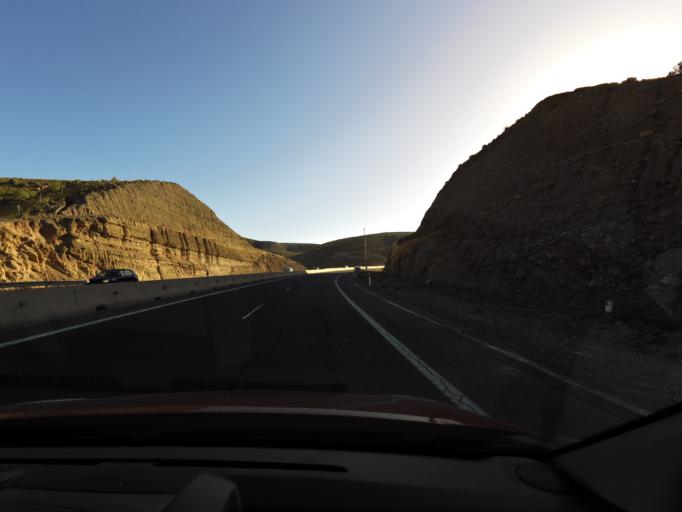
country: ES
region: Canary Islands
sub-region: Provincia de Las Palmas
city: Puerto Rico
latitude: 27.7707
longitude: -15.6561
